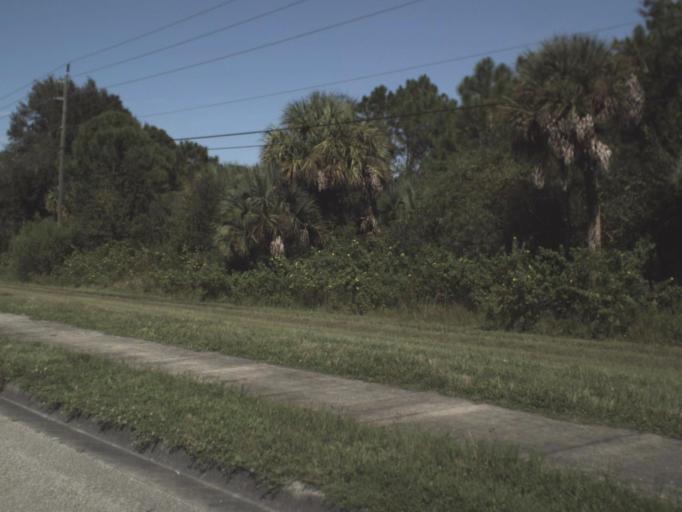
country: US
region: Florida
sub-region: Sarasota County
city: North Port
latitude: 26.9884
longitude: -82.2054
